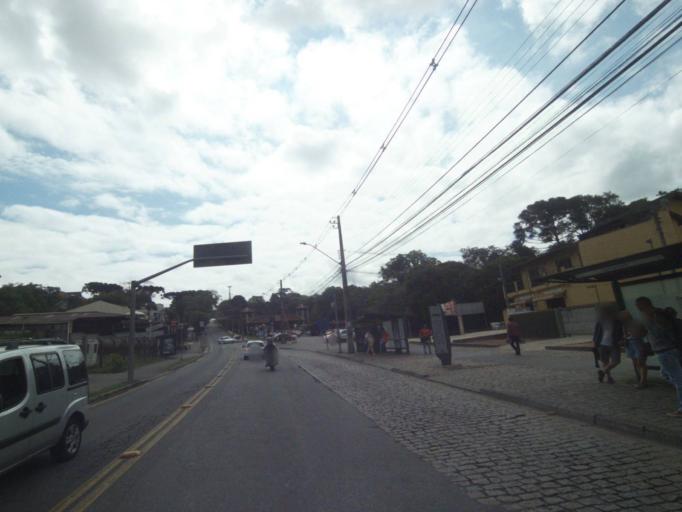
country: BR
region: Parana
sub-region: Curitiba
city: Curitiba
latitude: -25.3856
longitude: -49.2751
